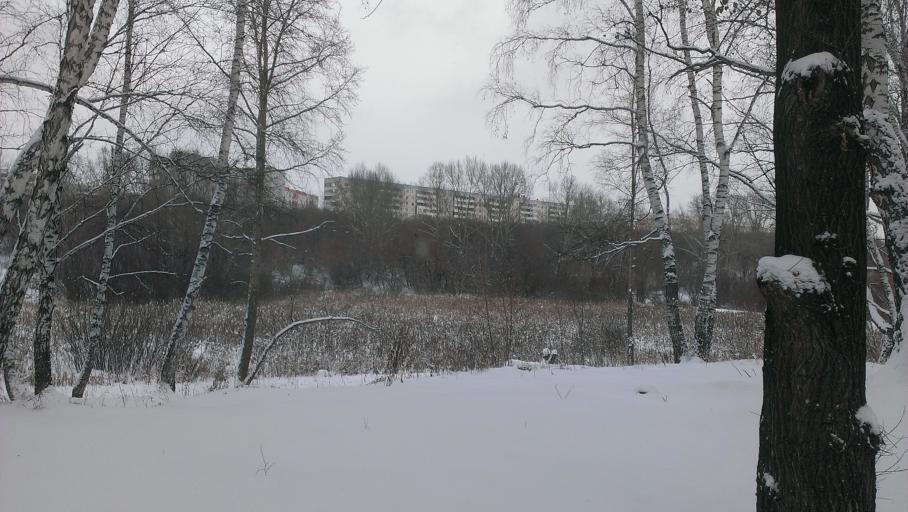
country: RU
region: Altai Krai
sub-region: Gorod Barnaulskiy
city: Barnaul
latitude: 53.3697
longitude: 83.7214
